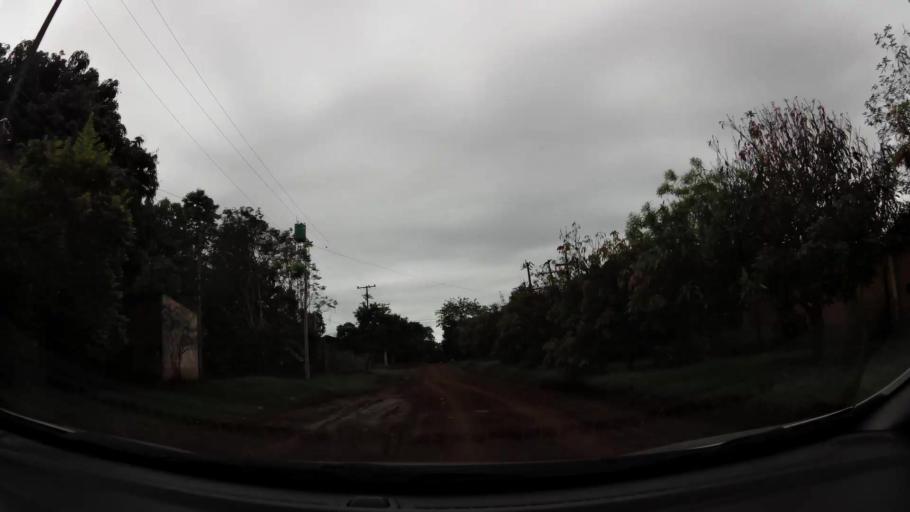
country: PY
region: Alto Parana
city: Ciudad del Este
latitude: -25.4381
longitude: -54.6392
